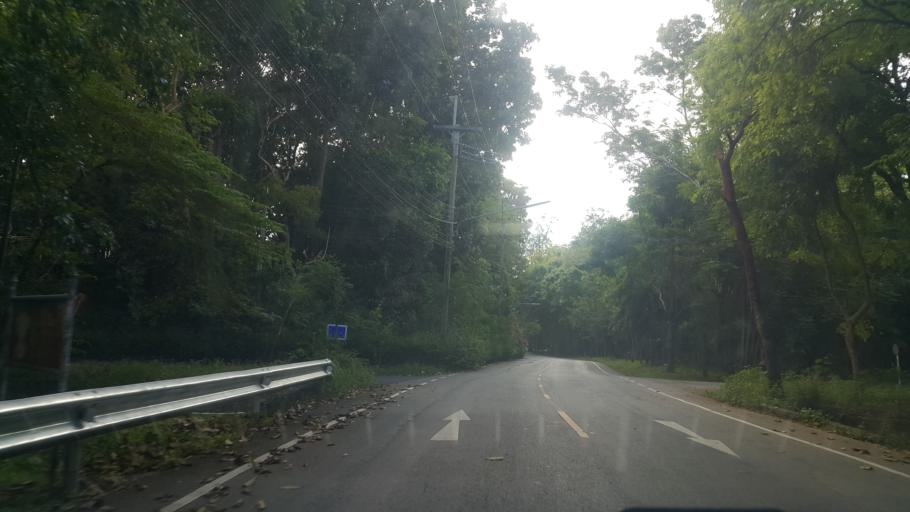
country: TH
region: Rayong
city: Ban Chang
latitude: 12.7867
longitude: 100.9607
